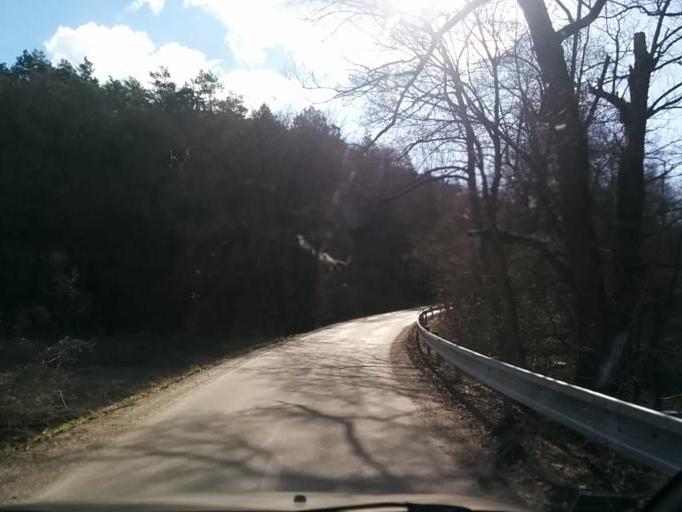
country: SK
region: Nitriansky
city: Cachtice
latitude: 48.7361
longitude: 17.7605
